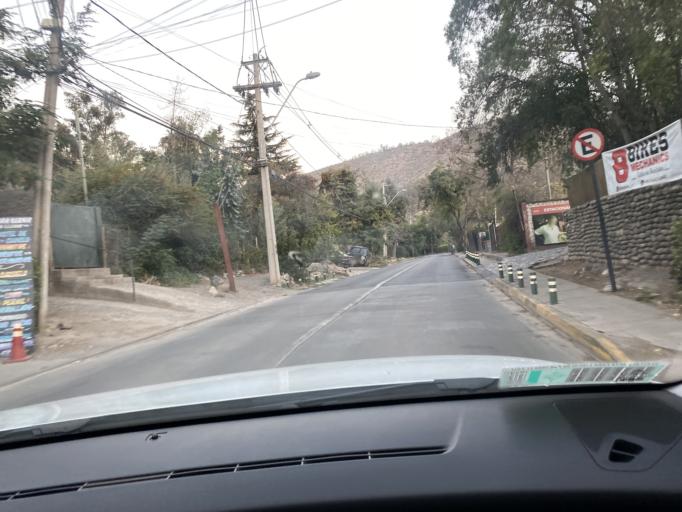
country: CL
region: Santiago Metropolitan
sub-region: Provincia de Santiago
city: Villa Presidente Frei, Nunoa, Santiago, Chile
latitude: -33.3612
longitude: -70.4922
